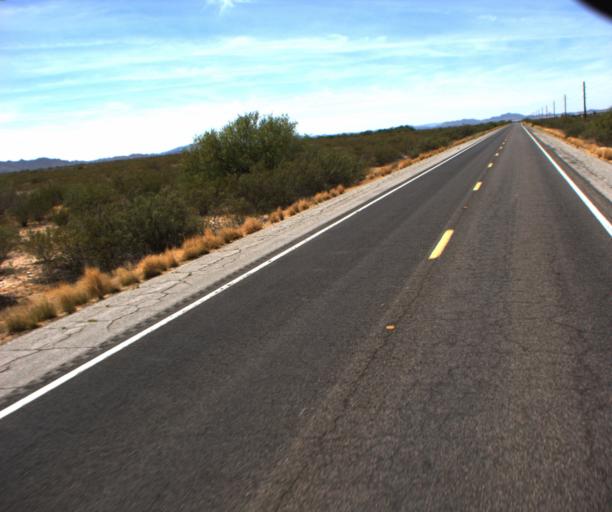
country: US
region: Arizona
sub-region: La Paz County
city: Salome
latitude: 33.8401
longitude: -113.4803
